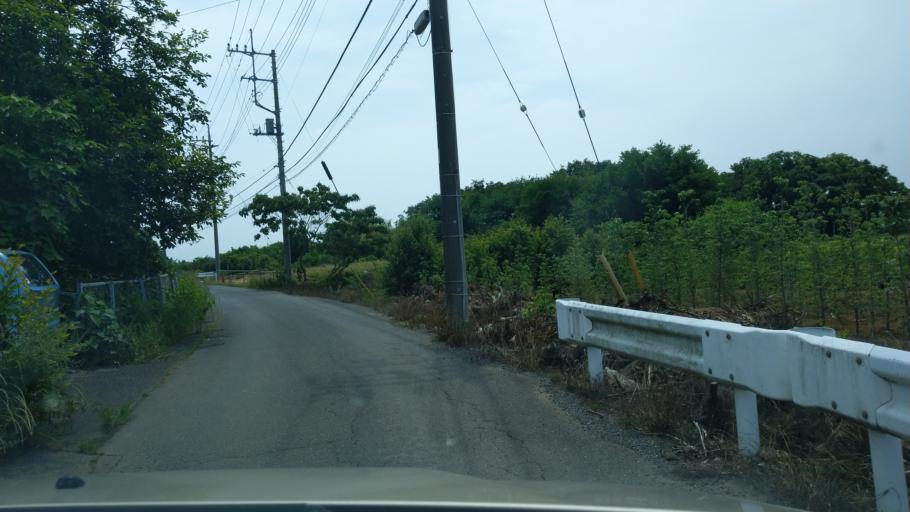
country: JP
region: Saitama
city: Saitama
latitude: 35.8978
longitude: 139.6877
